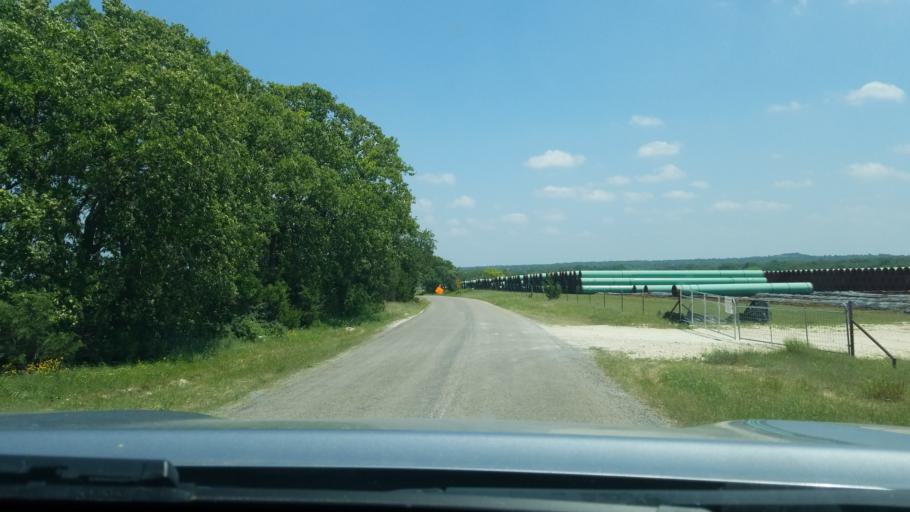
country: US
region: Texas
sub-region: Blanco County
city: Blanco
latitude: 30.0770
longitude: -98.3989
